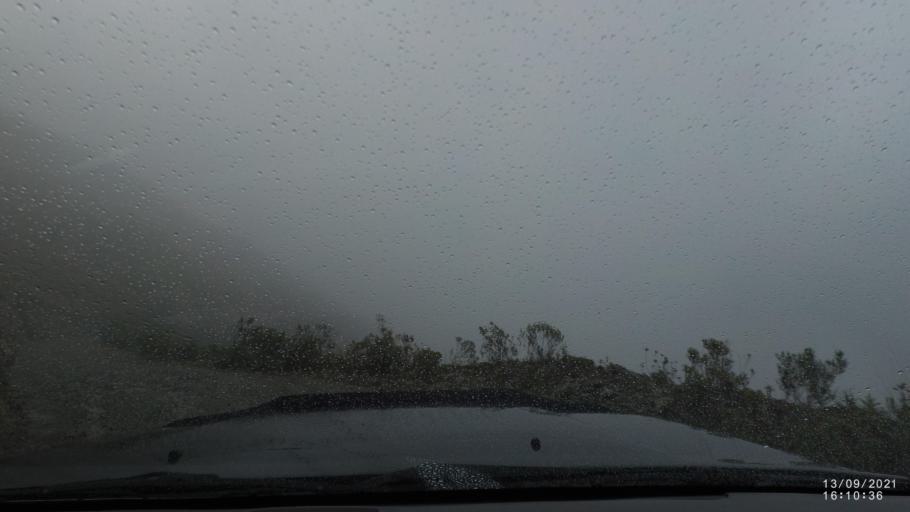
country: BO
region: Cochabamba
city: Colomi
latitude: -17.2782
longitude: -65.7107
